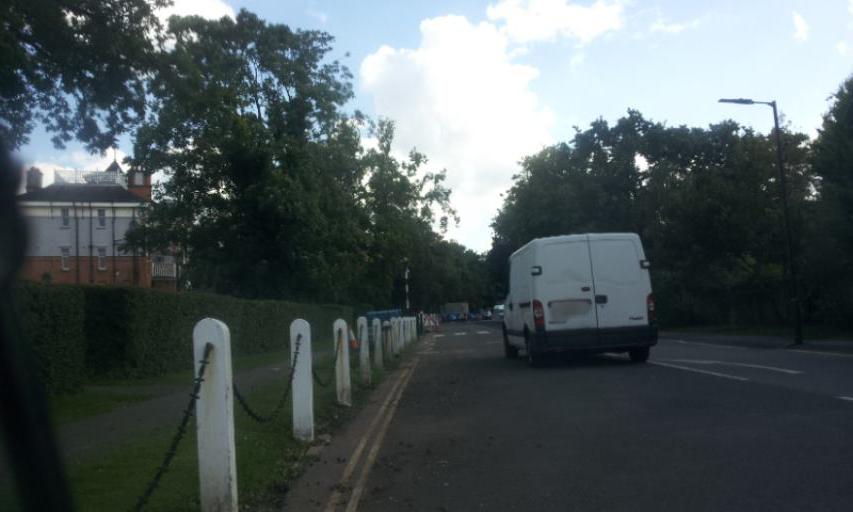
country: GB
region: England
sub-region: Greater London
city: Brixton
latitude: 51.4361
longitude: -0.0807
